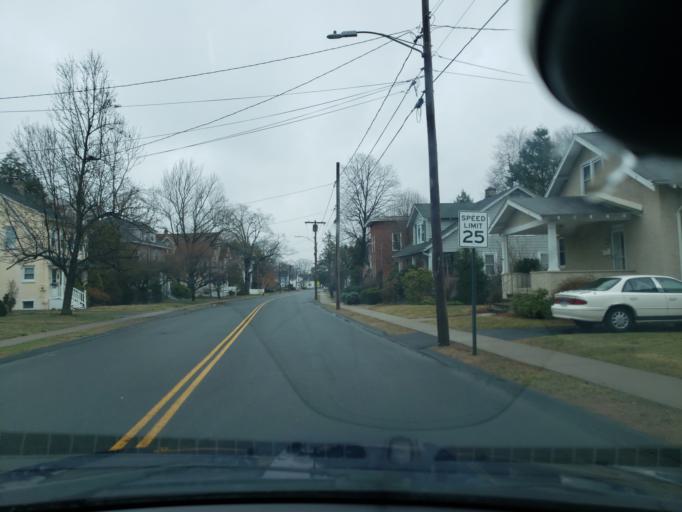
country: US
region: Connecticut
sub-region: Hartford County
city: Windsor
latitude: 41.8515
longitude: -72.6501
